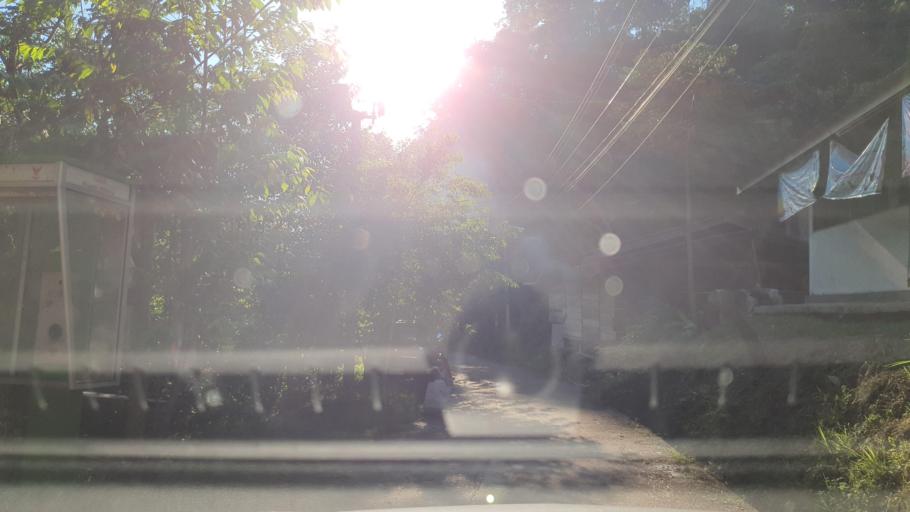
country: TH
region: Chiang Mai
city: Mae On
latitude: 18.8161
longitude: 99.3401
